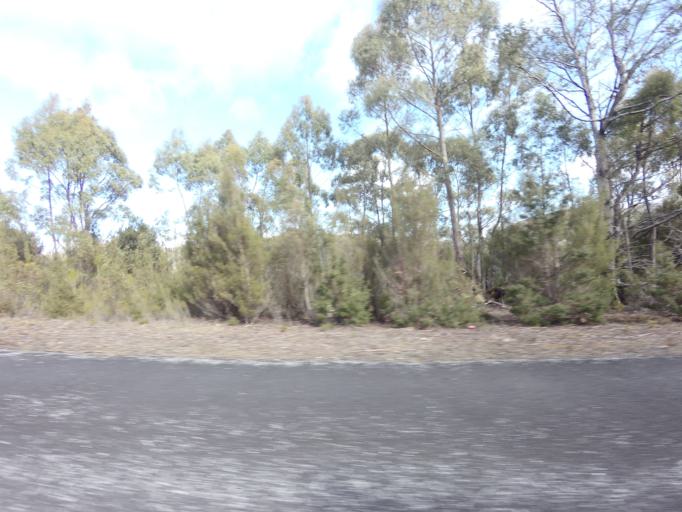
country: AU
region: Tasmania
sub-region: Huon Valley
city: Geeveston
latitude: -42.8088
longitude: 146.0970
